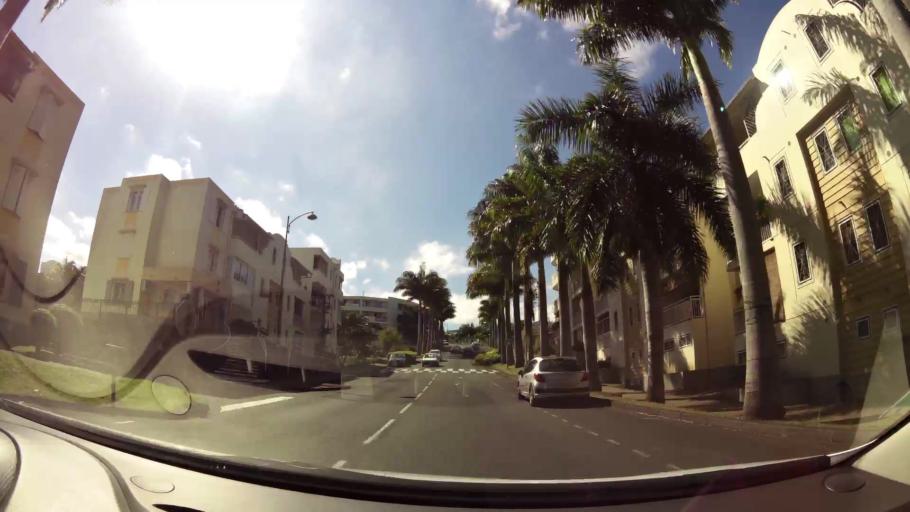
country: RE
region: Reunion
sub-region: Reunion
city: Le Tampon
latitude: -21.2765
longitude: 55.5041
